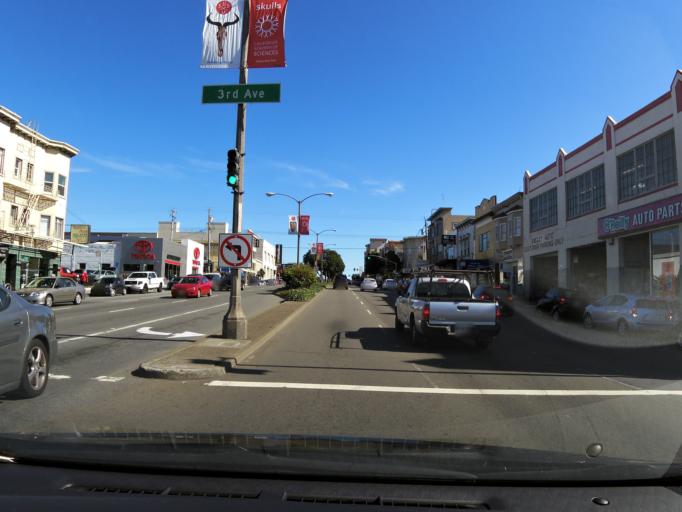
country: US
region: California
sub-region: San Francisco County
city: San Francisco
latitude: 37.7811
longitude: -122.4611
